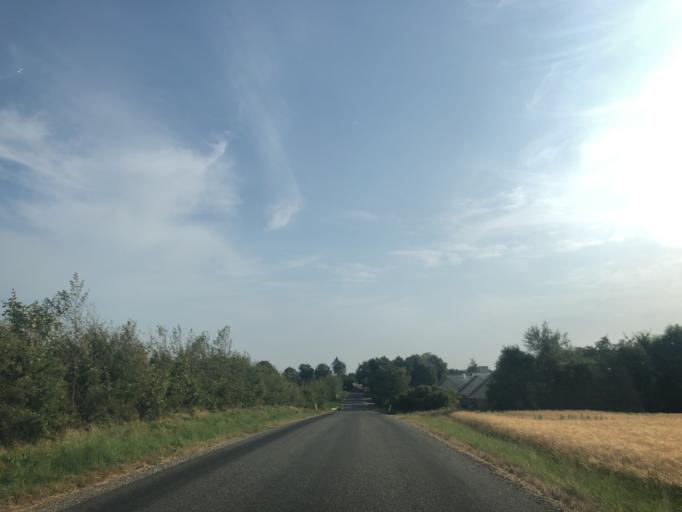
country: DK
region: Central Jutland
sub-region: Skive Kommune
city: Skive
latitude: 56.7232
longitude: 9.0232
